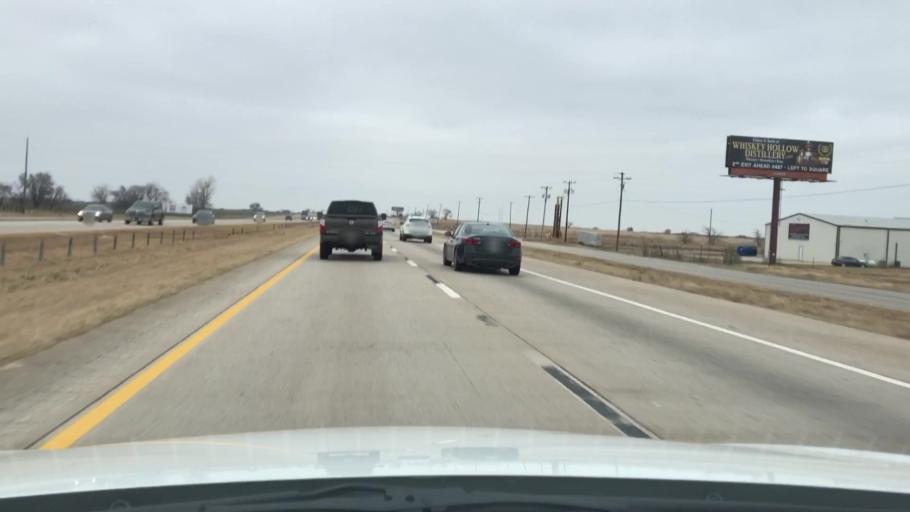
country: US
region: Texas
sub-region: Denton County
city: Sanger
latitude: 33.4458
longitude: -97.1641
